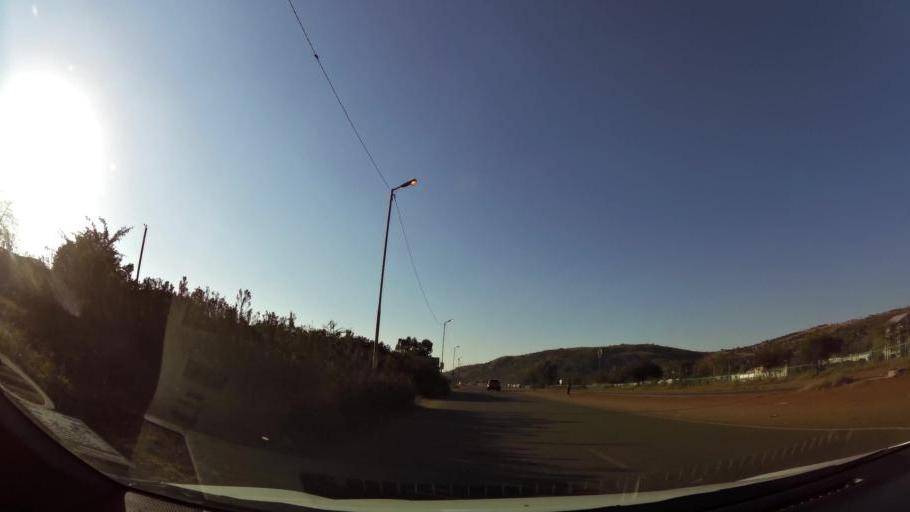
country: ZA
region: Gauteng
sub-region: City of Tshwane Metropolitan Municipality
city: Cullinan
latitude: -25.7013
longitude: 28.4190
